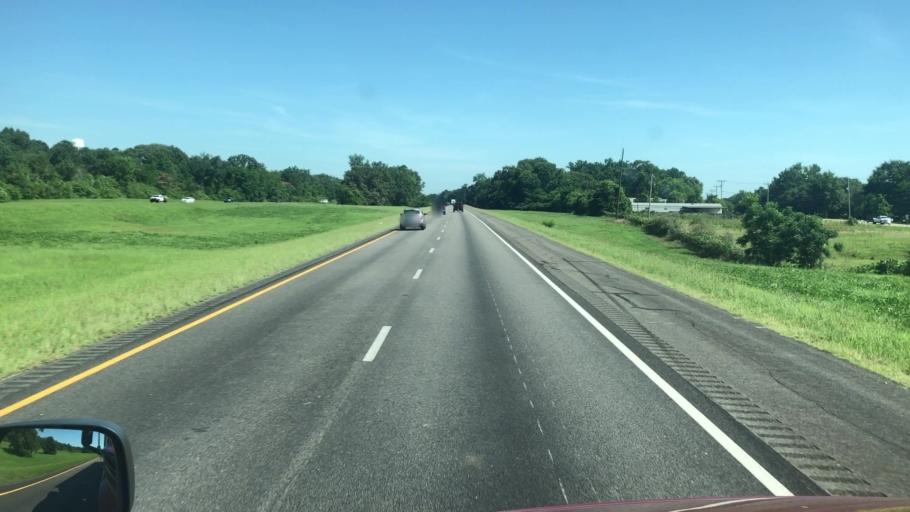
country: US
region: Alabama
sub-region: Autauga County
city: Pine Level
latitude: 32.5666
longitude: -86.4646
